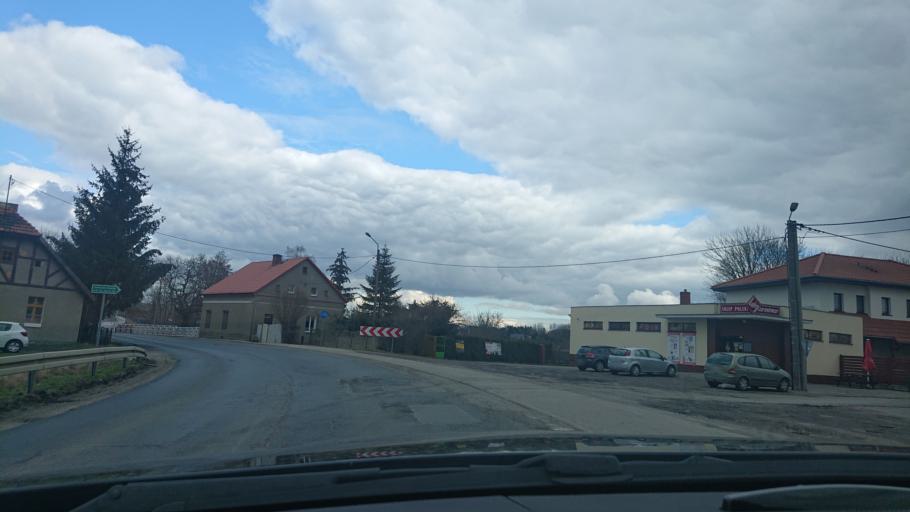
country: PL
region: Greater Poland Voivodeship
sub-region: Powiat gnieznienski
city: Niechanowo
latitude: 52.5509
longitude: 17.6933
